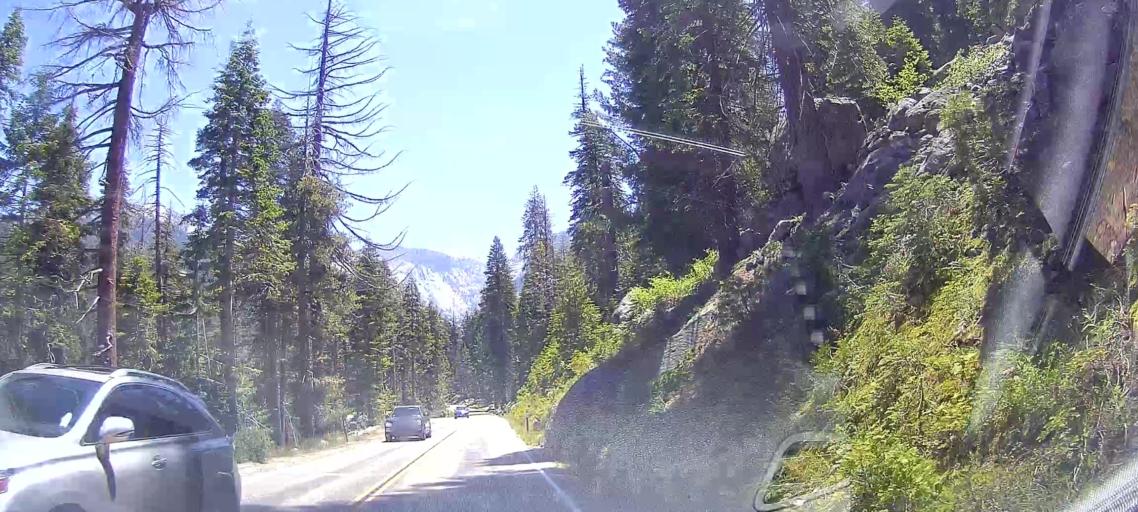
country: US
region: California
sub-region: Tulare County
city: Three Rivers
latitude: 36.6022
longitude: -118.7397
